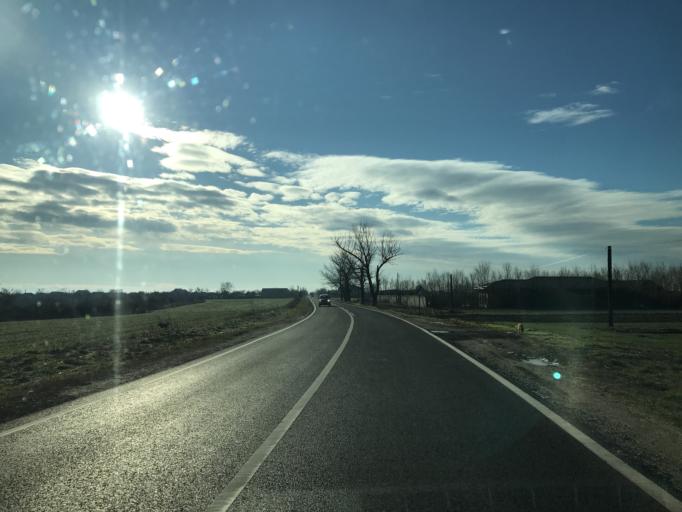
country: RO
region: Olt
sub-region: Comuna Ganeasa
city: Ganeasa
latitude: 44.3938
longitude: 24.2806
